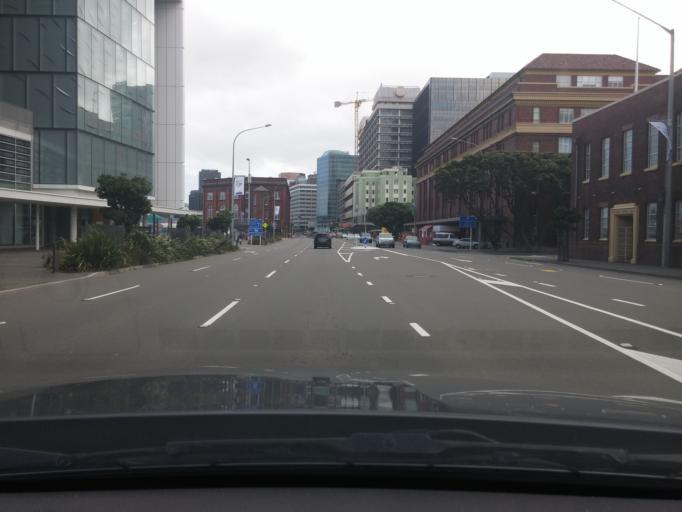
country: NZ
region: Wellington
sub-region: Wellington City
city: Wellington
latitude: -41.2788
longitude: 174.7818
